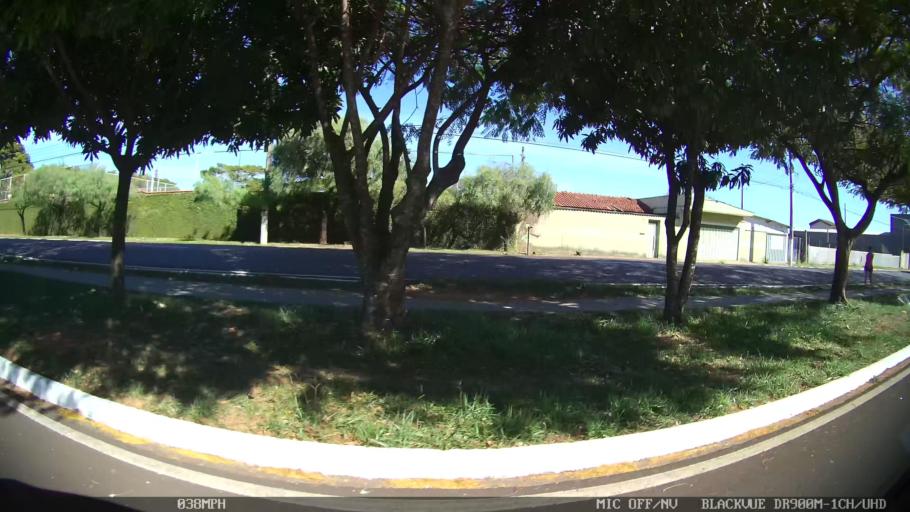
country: BR
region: Sao Paulo
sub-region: Franca
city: Franca
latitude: -20.5563
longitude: -47.3600
